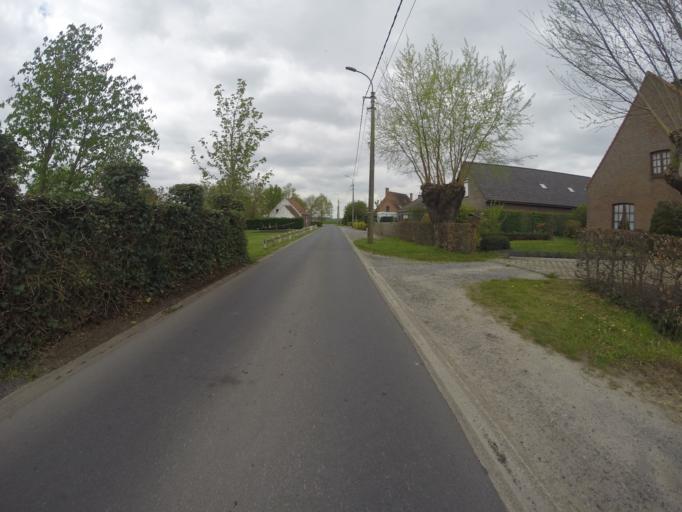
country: BE
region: Flanders
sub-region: Provincie Oost-Vlaanderen
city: Aalter
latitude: 51.0488
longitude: 3.4557
